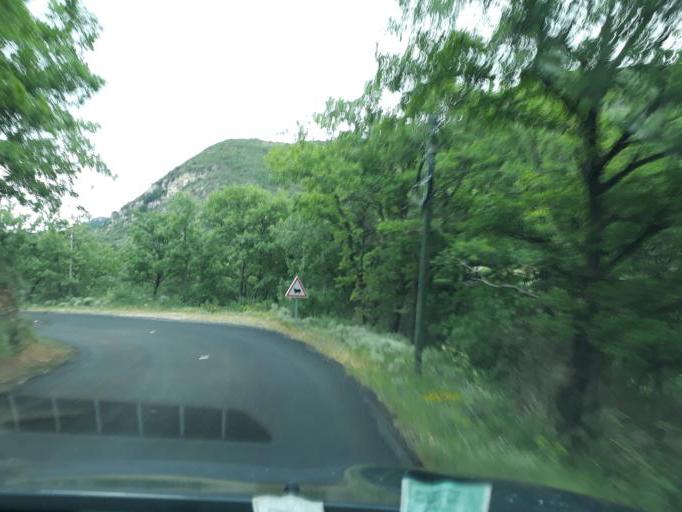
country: FR
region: Languedoc-Roussillon
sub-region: Departement de l'Herault
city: Lodeve
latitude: 43.7728
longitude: 3.2992
